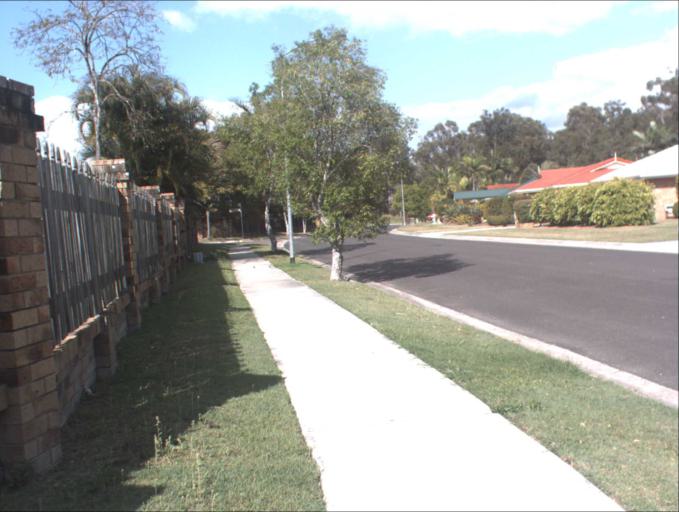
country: AU
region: Queensland
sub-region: Logan
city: Park Ridge South
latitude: -27.6765
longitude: 153.0555
